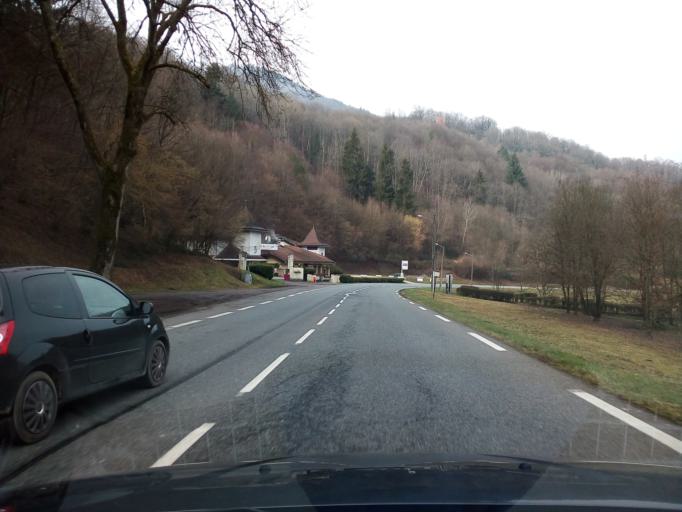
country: FR
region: Rhone-Alpes
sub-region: Departement de l'Isere
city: Herbeys
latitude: 45.1492
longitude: 5.8263
